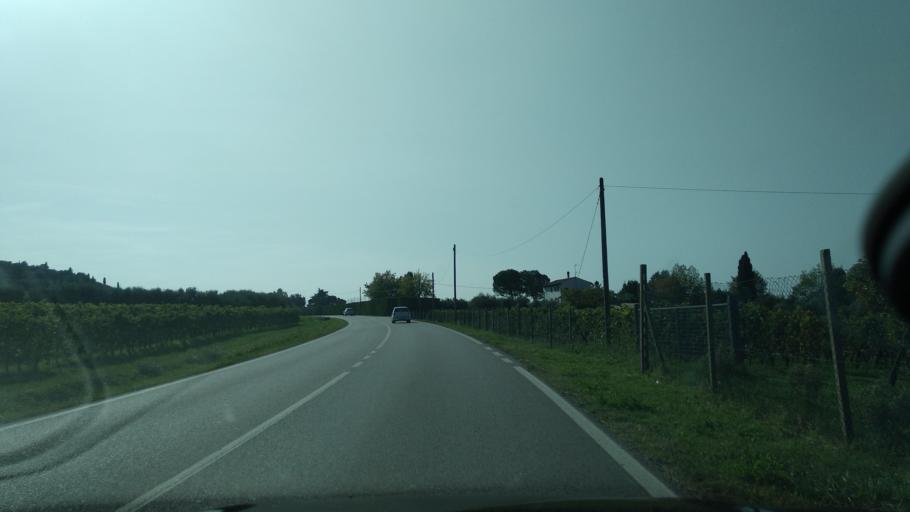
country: IT
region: Veneto
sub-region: Provincia di Verona
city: Bardolino
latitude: 45.5366
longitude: 10.7455
